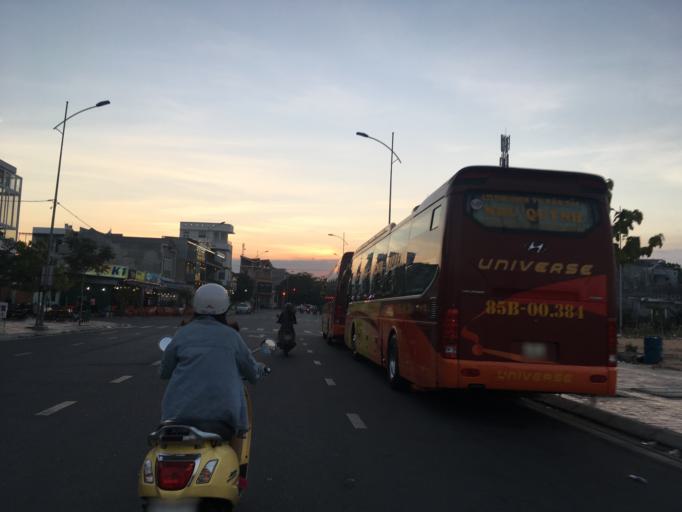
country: VN
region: Ninh Thuan
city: Phan Rang-Thap Cham
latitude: 11.5703
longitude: 108.9959
